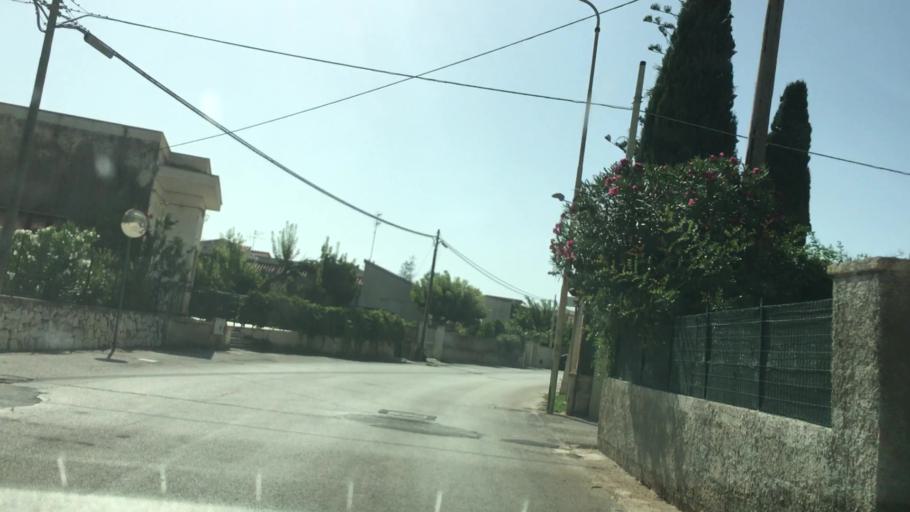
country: IT
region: Sicily
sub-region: Ragusa
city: Pozzallo
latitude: 36.7154
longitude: 14.7826
